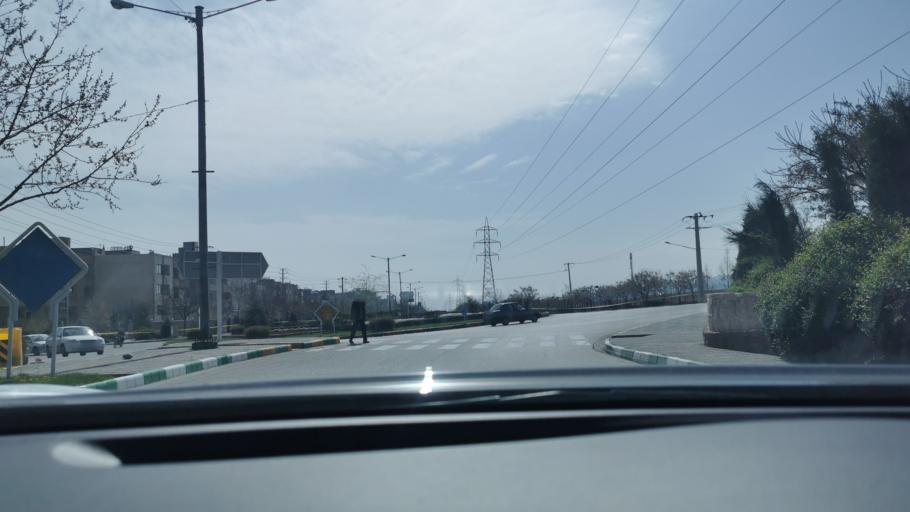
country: IR
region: Razavi Khorasan
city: Mashhad
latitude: 36.2885
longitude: 59.5339
